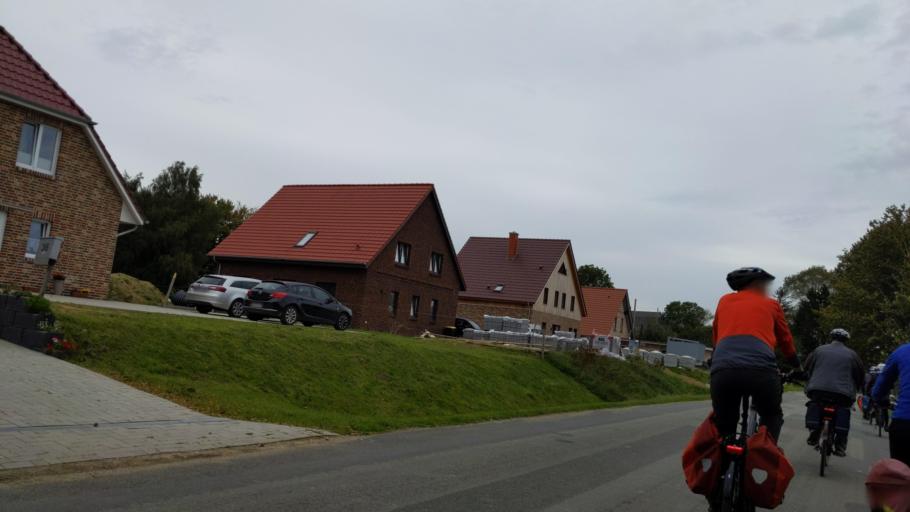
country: DE
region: Mecklenburg-Vorpommern
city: Schlagsdorf
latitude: 53.7580
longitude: 10.8276
